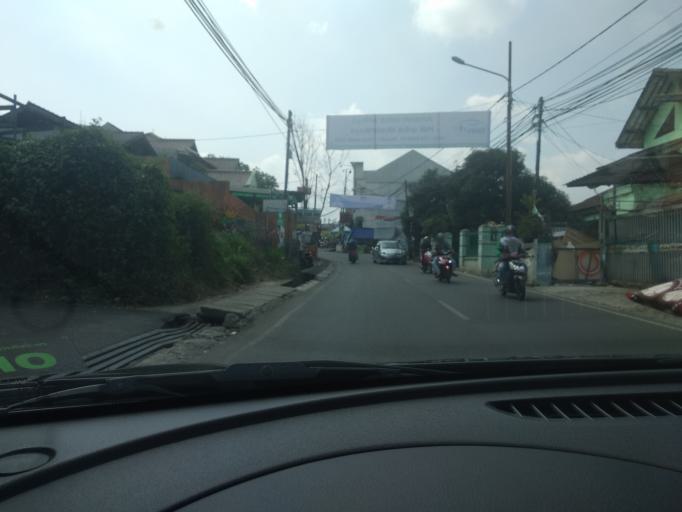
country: ID
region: West Java
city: Cimahi
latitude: -6.8933
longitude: 107.5620
